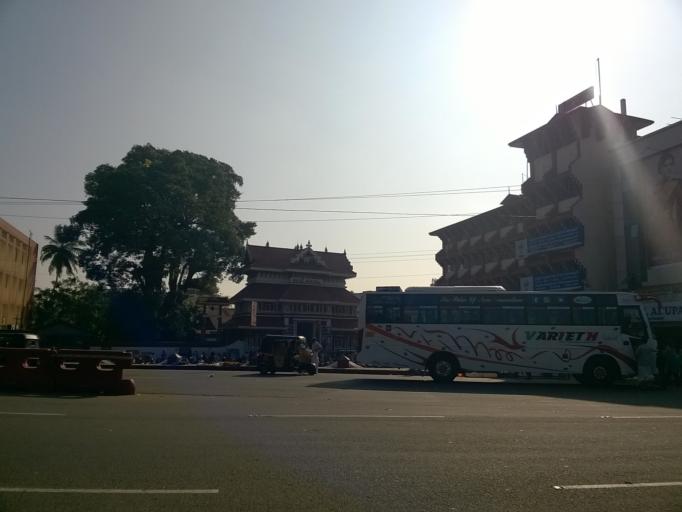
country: IN
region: Kerala
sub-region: Thrissur District
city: Trichur
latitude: 10.5248
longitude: 76.2168
